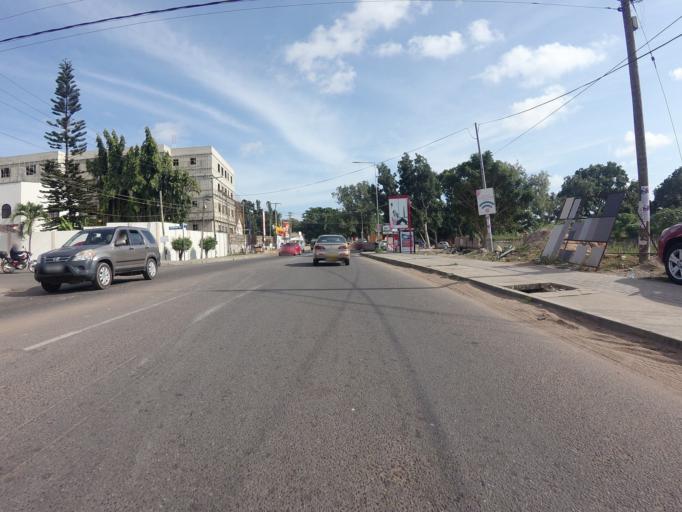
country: GH
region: Greater Accra
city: Medina Estates
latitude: 5.6412
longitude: -0.1621
